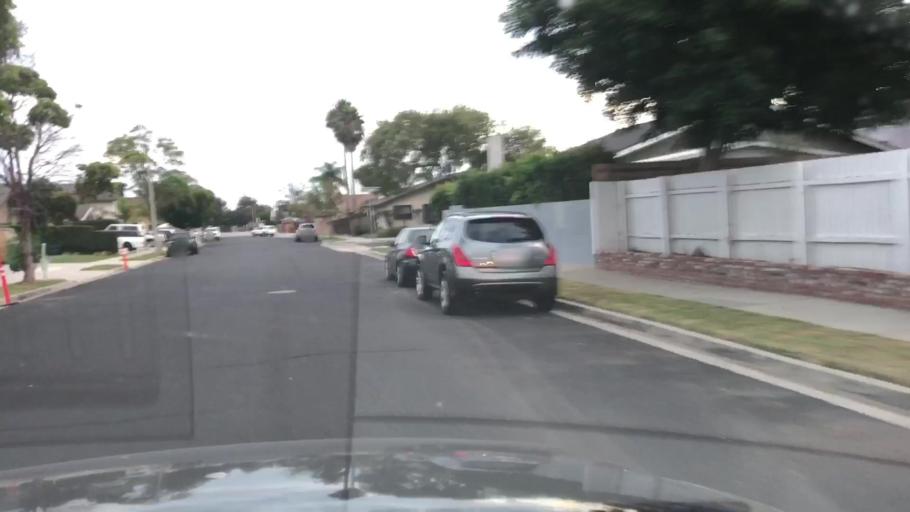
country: US
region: California
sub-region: Ventura County
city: Channel Islands Beach
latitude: 34.1859
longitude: -119.2089
